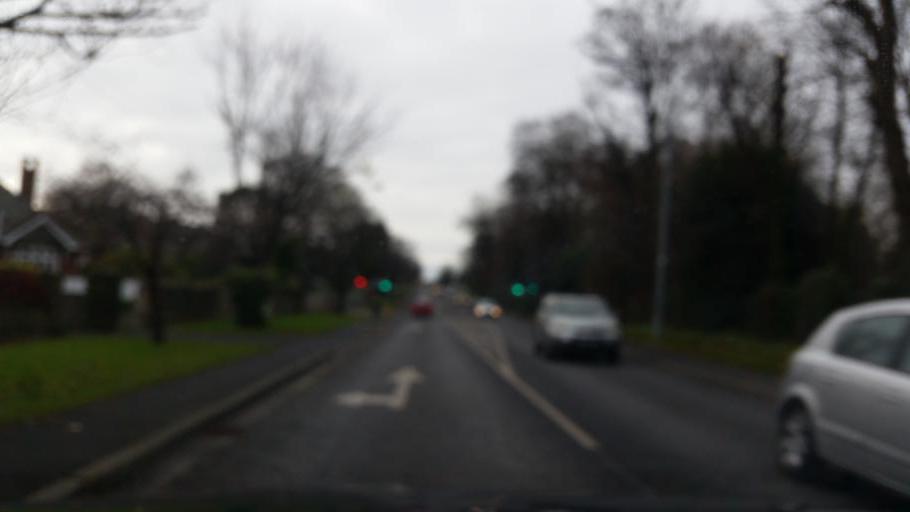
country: IE
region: Leinster
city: Mount Merrion
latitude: 53.3019
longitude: -6.2129
